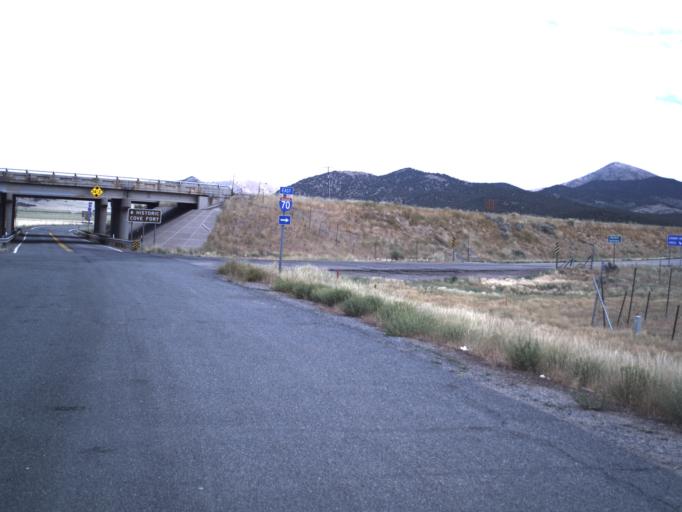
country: US
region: Utah
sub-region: Beaver County
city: Beaver
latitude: 38.5859
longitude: -112.5845
